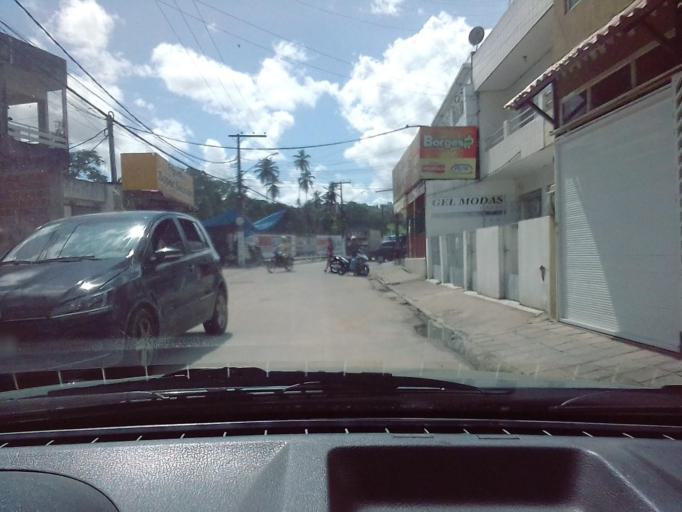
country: BR
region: Pernambuco
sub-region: Vitoria De Santo Antao
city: Vitoria de Santo Antao
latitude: -8.1144
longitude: -35.2999
